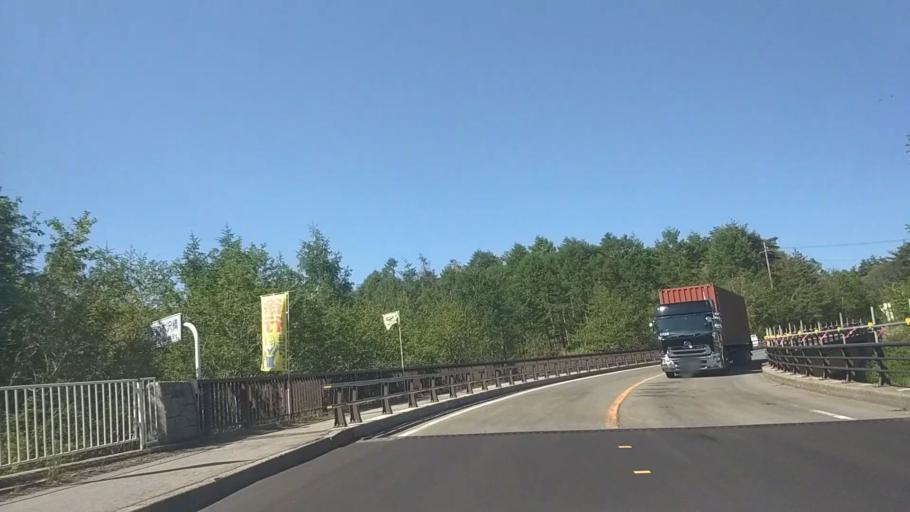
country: JP
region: Yamanashi
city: Nirasaki
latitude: 35.9253
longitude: 138.4395
